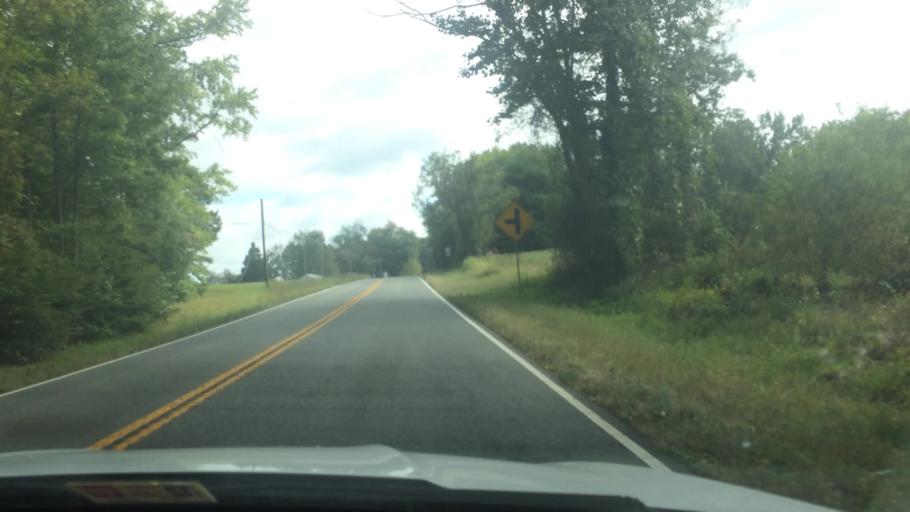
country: US
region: Virginia
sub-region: Northumberland County
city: Heathsville
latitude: 37.8483
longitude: -76.5824
